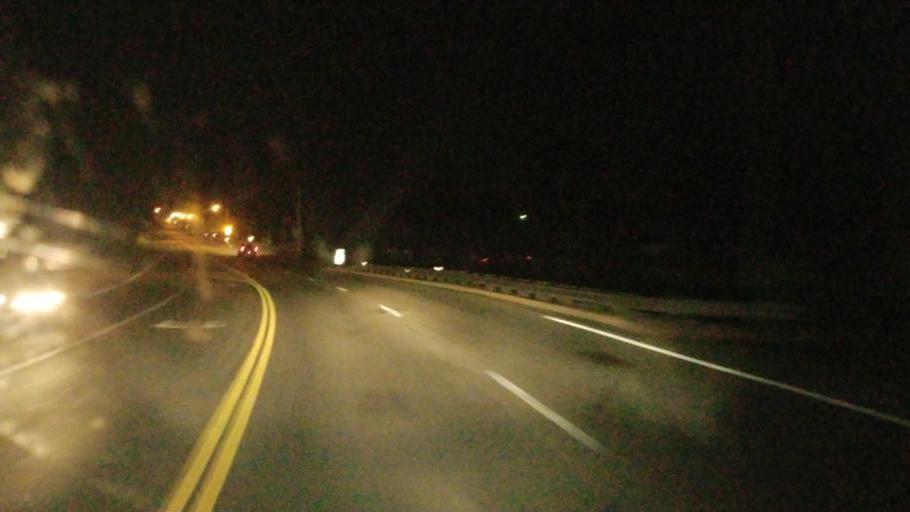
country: US
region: Ohio
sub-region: Ashland County
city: Loudonville
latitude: 40.6295
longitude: -82.2339
